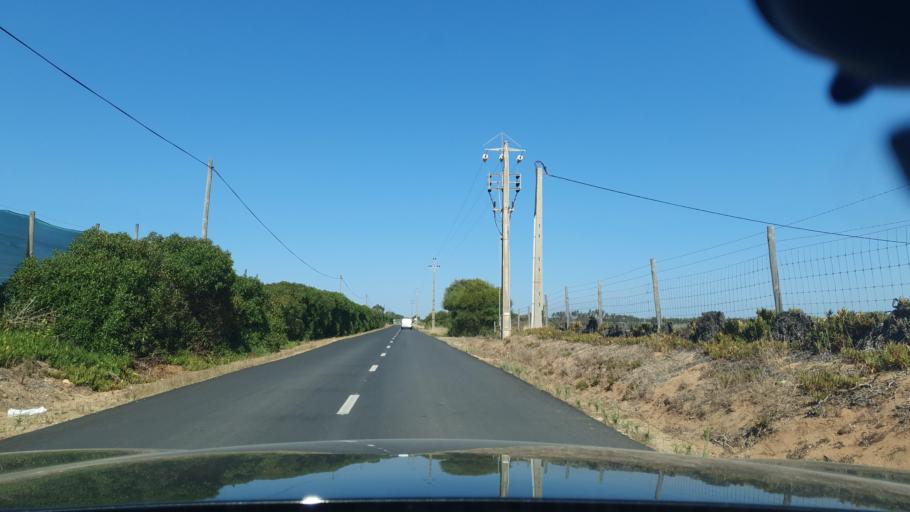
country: PT
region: Beja
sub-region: Odemira
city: Sao Teotonio
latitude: 37.4649
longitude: -8.7935
